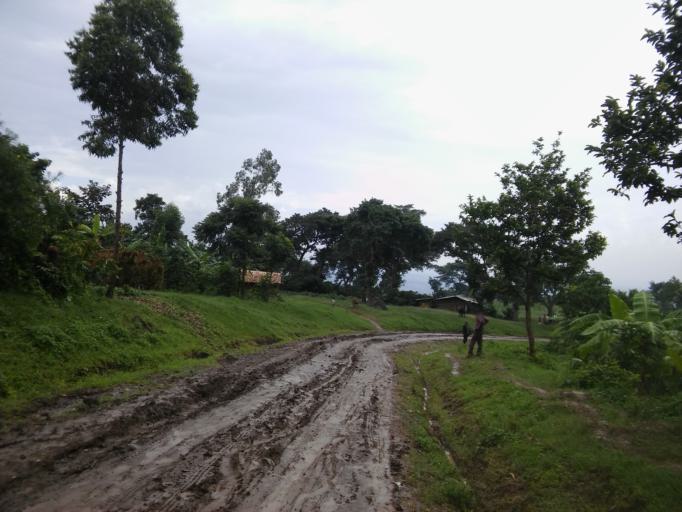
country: UG
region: Eastern Region
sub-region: Mbale District
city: Mbale
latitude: 1.0130
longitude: 34.2292
